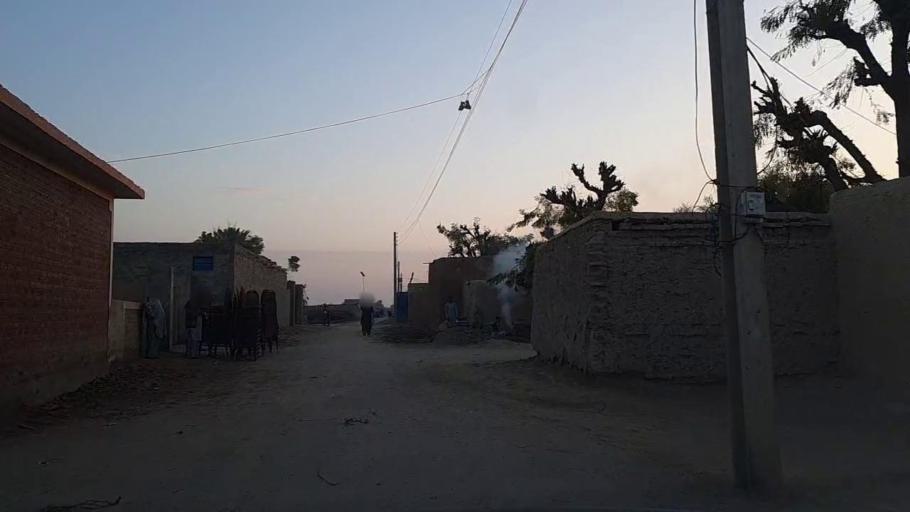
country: PK
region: Sindh
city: Jam Sahib
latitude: 26.4628
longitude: 68.5219
